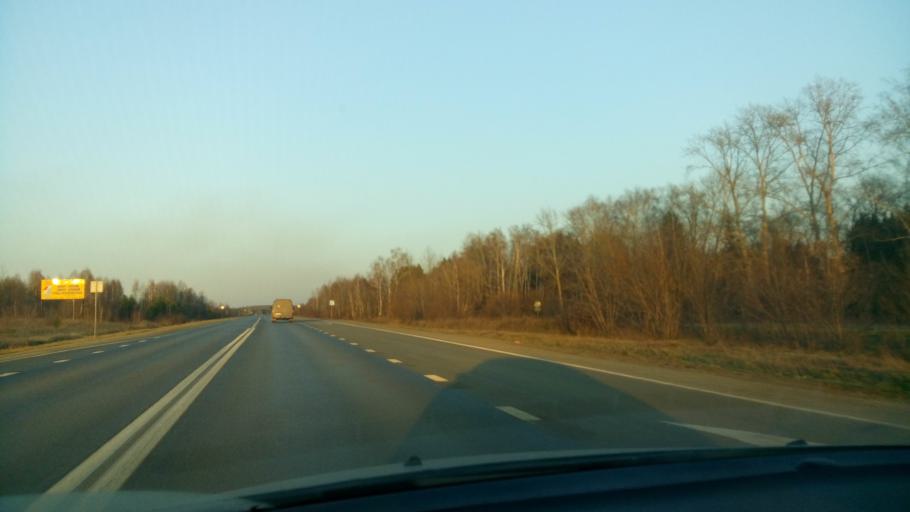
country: RU
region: Sverdlovsk
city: Obukhovskoye
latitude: 56.8457
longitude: 62.5935
